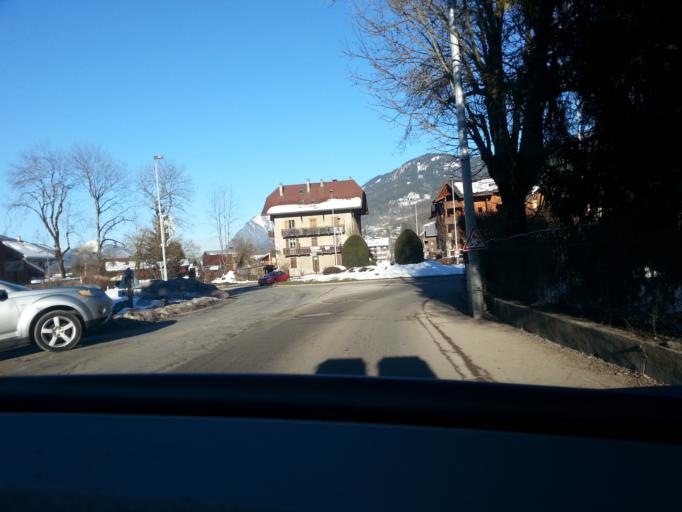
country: FR
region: Rhone-Alpes
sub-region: Departement de la Haute-Savoie
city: Samoens
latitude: 46.0803
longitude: 6.7277
